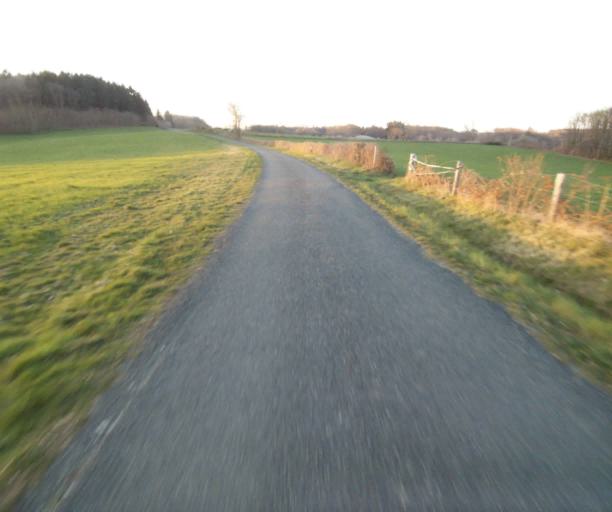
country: FR
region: Limousin
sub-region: Departement de la Correze
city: Uzerche
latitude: 45.3745
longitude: 1.6079
